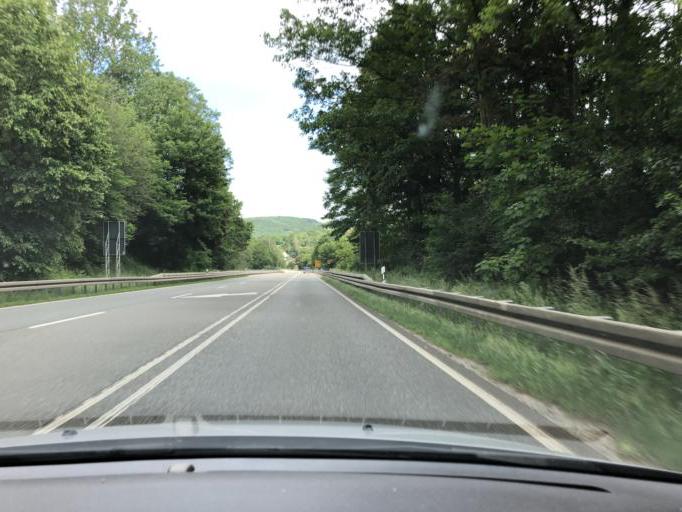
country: DE
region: Hesse
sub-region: Regierungsbezirk Kassel
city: Sontra
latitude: 51.0747
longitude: 9.9306
